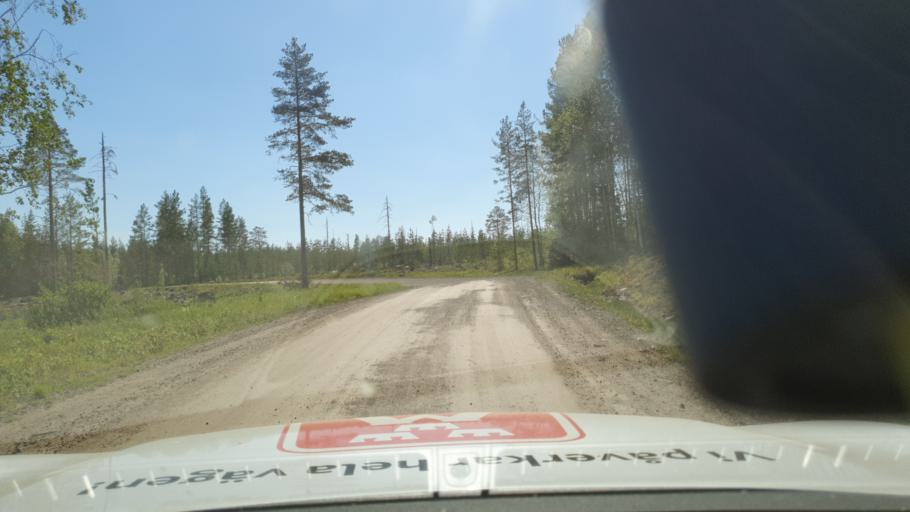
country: SE
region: Vaesterbotten
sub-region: Robertsfors Kommun
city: Robertsfors
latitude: 64.3732
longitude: 20.9949
